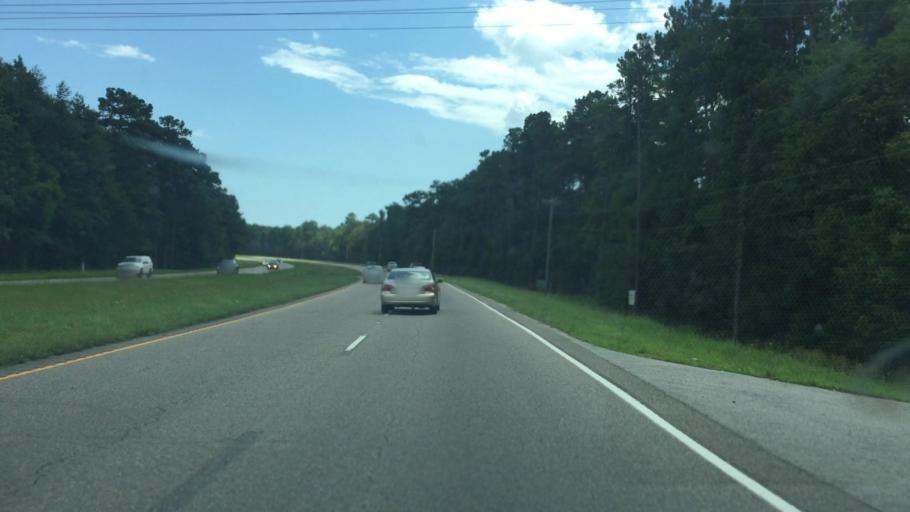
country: US
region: South Carolina
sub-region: Horry County
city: North Myrtle Beach
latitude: 33.9220
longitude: -78.7255
